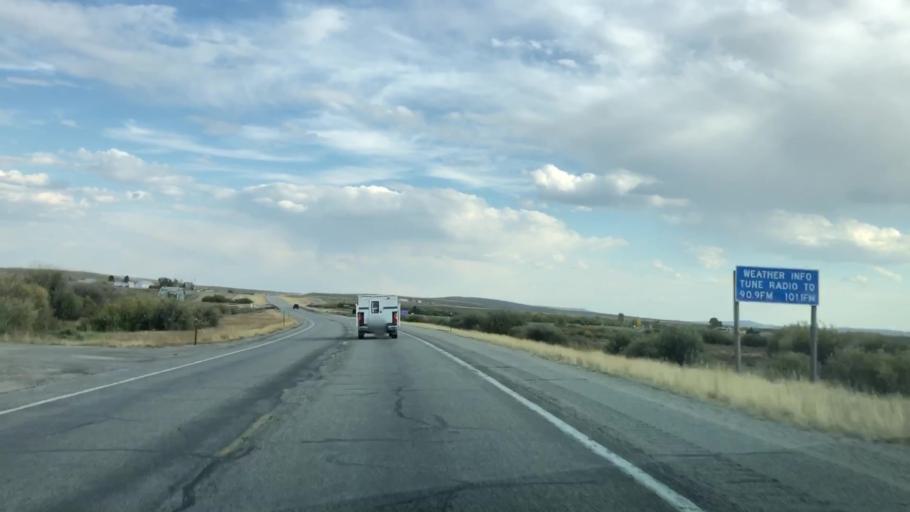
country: US
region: Wyoming
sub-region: Sublette County
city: Pinedale
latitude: 43.0211
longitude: -110.1217
